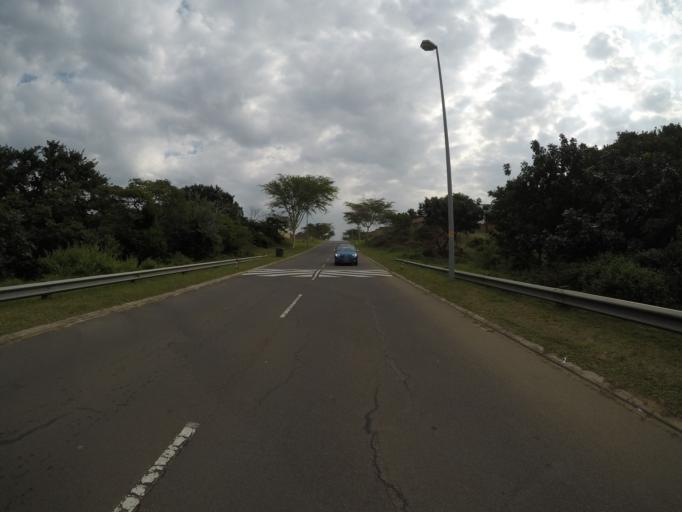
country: ZA
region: KwaZulu-Natal
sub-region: uThungulu District Municipality
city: Richards Bay
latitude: -28.7373
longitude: 32.0914
